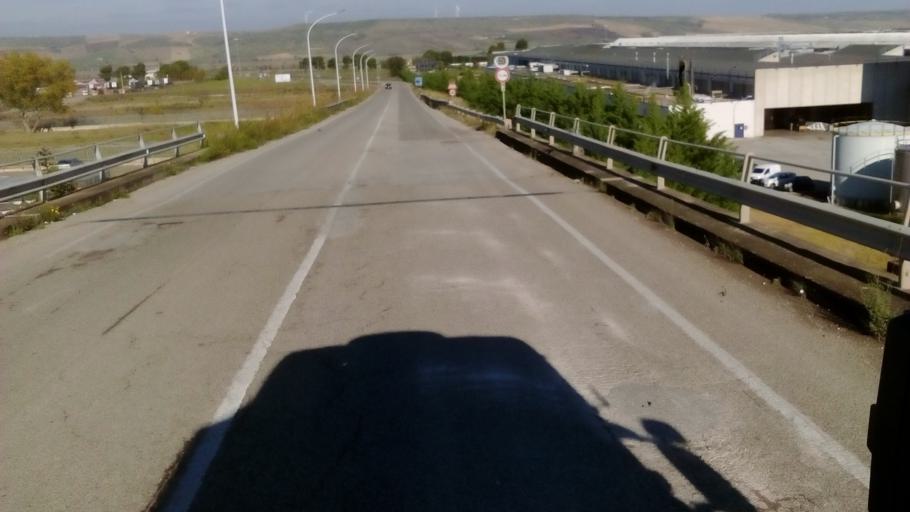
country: IT
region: Basilicate
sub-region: Provincia di Potenza
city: Melfi
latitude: 41.0722
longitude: 15.6905
